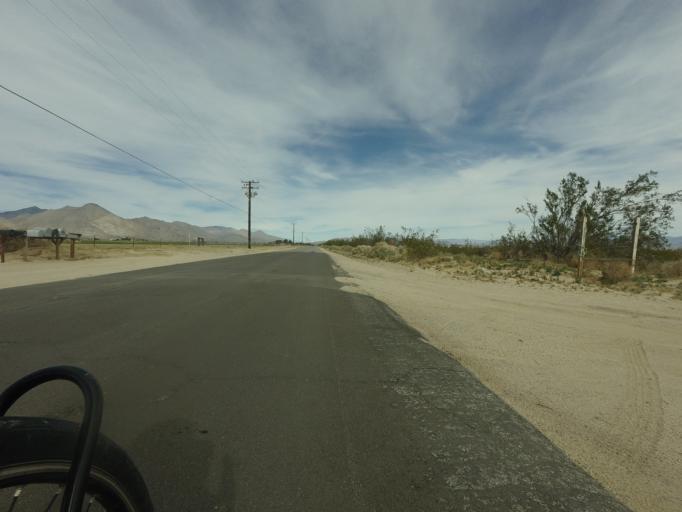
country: US
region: California
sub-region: Kern County
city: Inyokern
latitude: 35.7397
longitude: -117.8399
